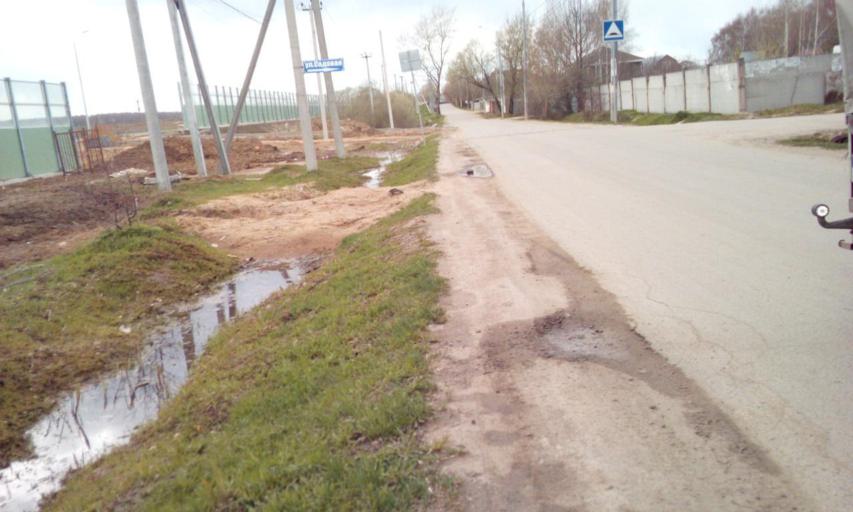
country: RU
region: Moskovskaya
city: Kommunarka
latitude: 55.5234
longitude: 37.4884
